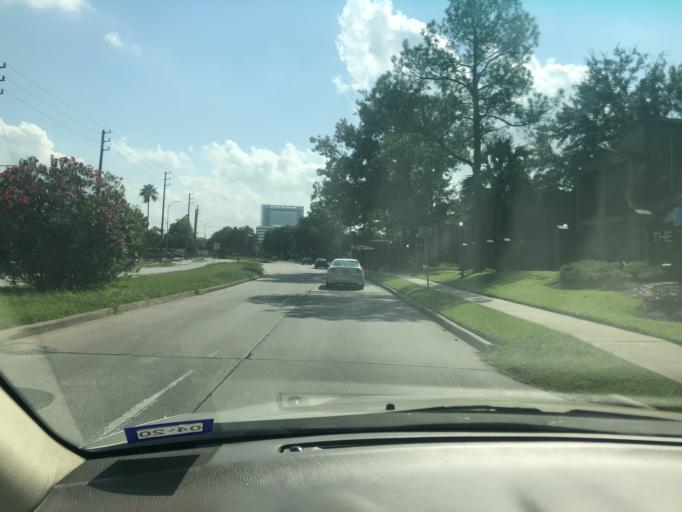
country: US
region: Texas
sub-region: Harris County
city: Bunker Hill Village
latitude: 29.7476
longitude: -95.5696
